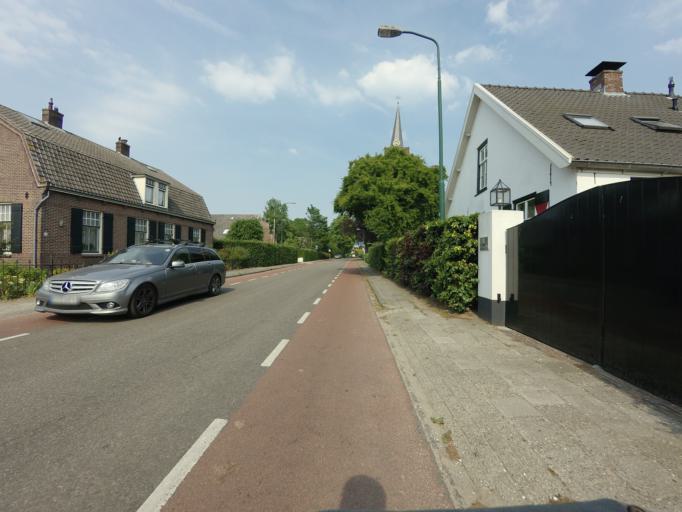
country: NL
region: North Holland
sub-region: Gemeente Wijdemeren
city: Nieuw-Loosdrecht
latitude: 52.1925
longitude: 5.1196
